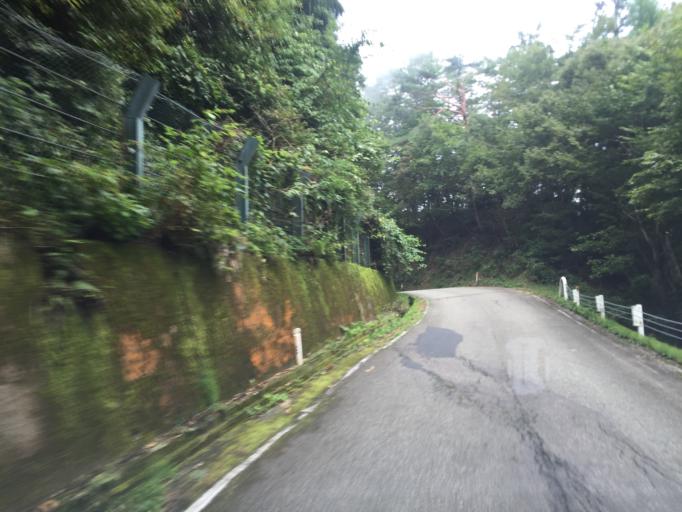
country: JP
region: Fukushima
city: Inawashiro
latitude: 37.4851
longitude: 139.9701
